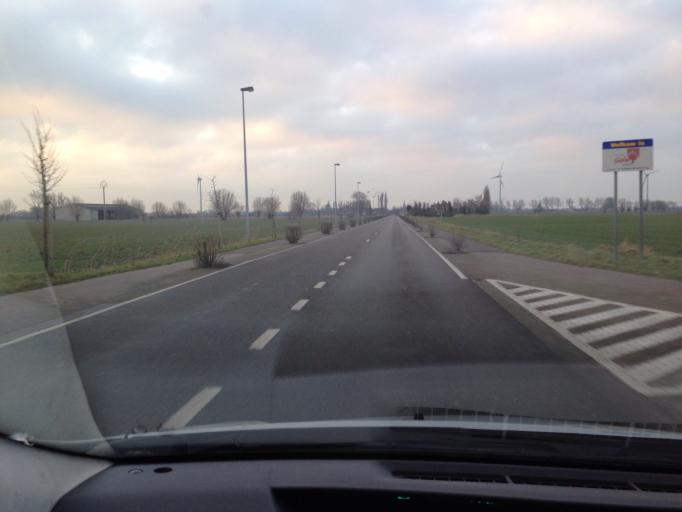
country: BE
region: Flanders
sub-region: Provincie West-Vlaanderen
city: Gistel
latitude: 51.1799
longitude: 2.9623
